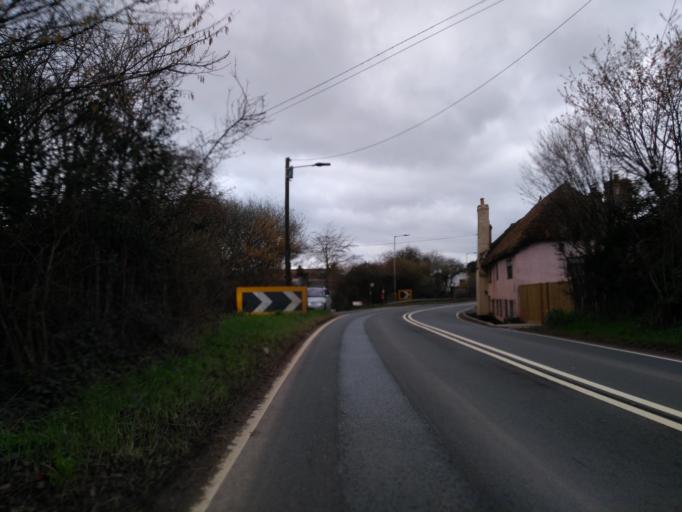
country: GB
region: England
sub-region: Devon
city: Crediton
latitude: 50.7760
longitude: -3.6086
